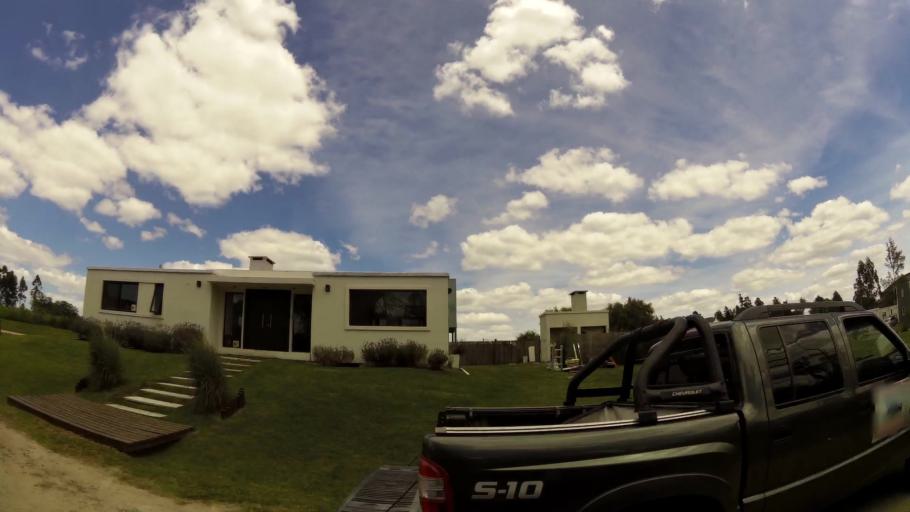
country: UY
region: Canelones
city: Colonia Nicolich
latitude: -34.8160
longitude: -55.9901
